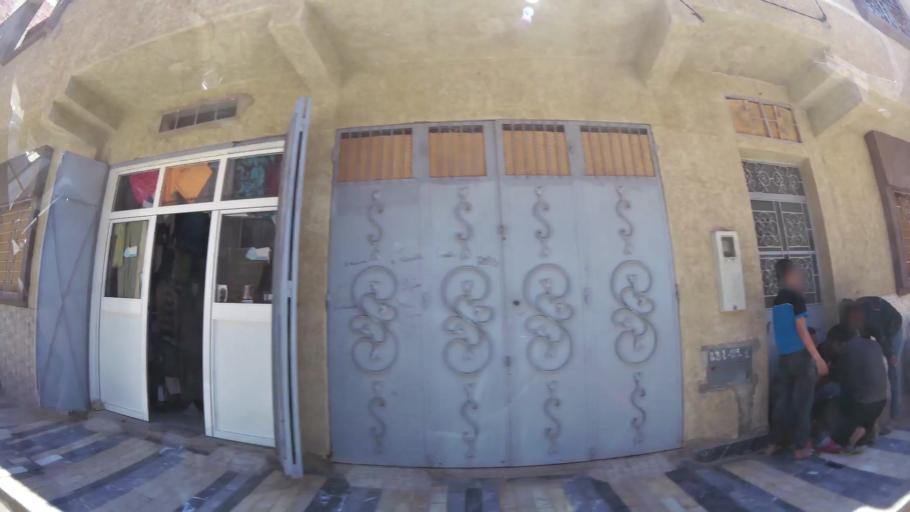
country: MA
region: Oriental
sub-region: Oujda-Angad
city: Oujda
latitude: 34.6624
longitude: -1.9251
